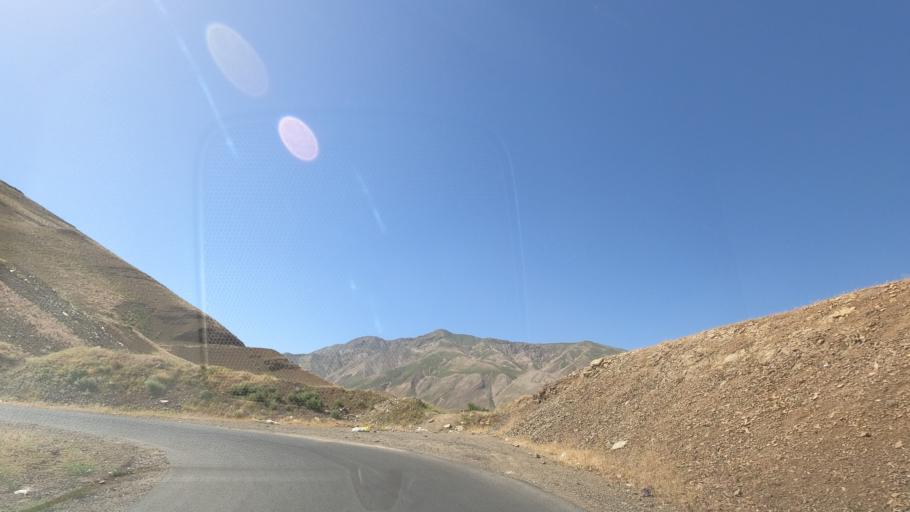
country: IR
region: Alborz
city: Karaj
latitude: 35.9384
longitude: 51.0791
